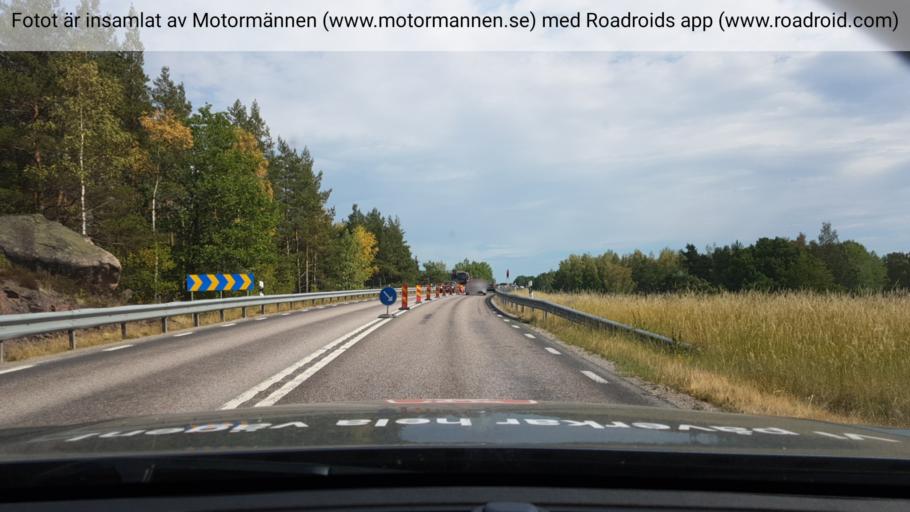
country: SE
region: Uppsala
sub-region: Enkopings Kommun
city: Orsundsbro
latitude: 59.8617
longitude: 17.3679
